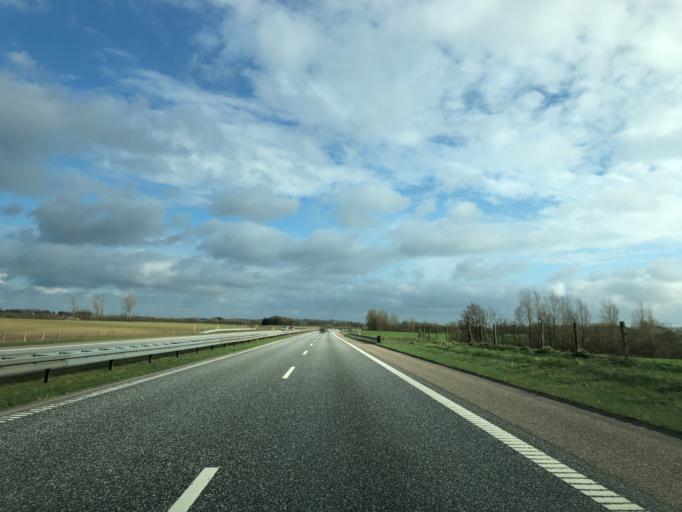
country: DK
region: North Denmark
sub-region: Alborg Kommune
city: Vestbjerg
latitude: 57.1935
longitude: 9.9364
